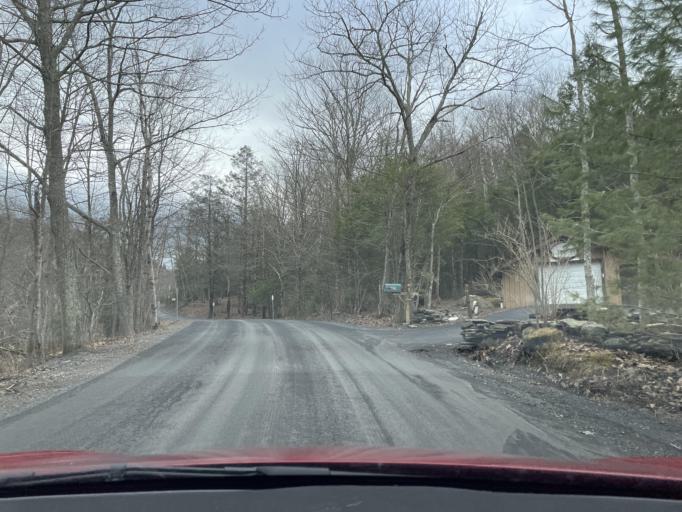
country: US
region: New York
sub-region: Ulster County
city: Woodstock
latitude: 42.0742
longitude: -74.1263
